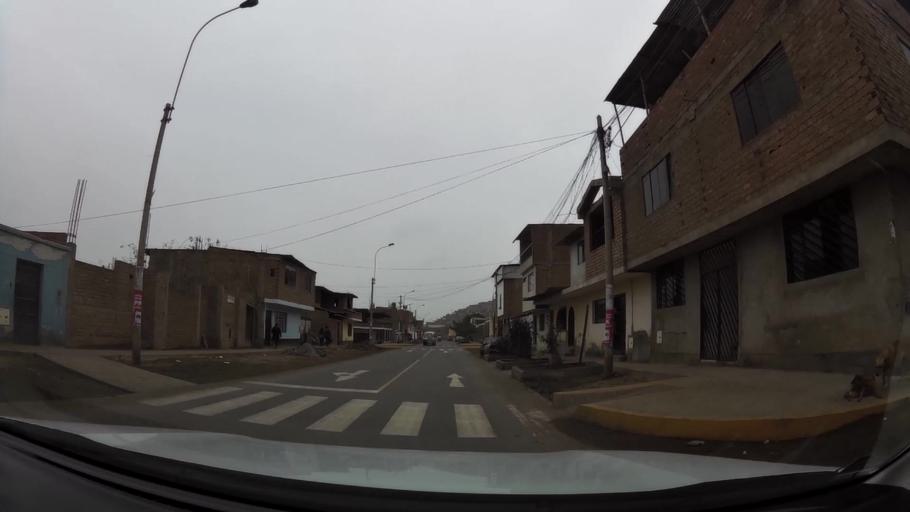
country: PE
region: Lima
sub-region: Lima
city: Surco
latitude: -12.2162
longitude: -76.9098
